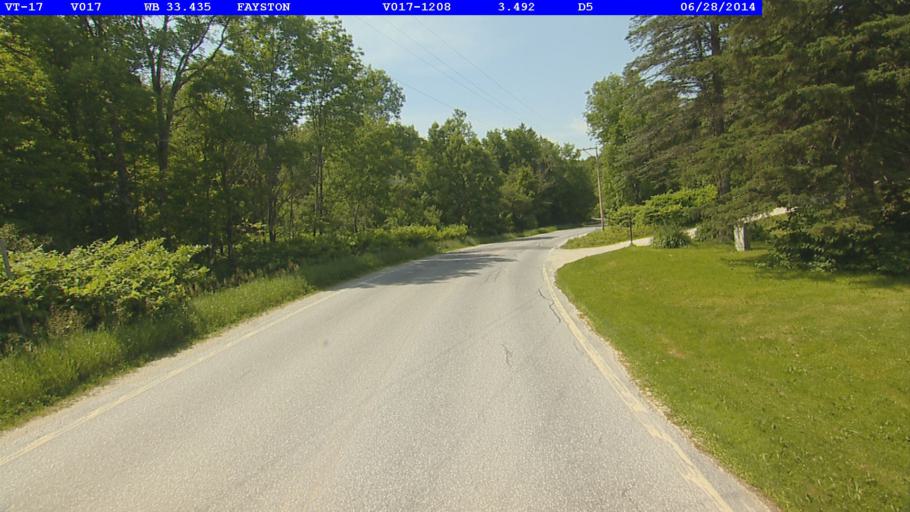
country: US
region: Vermont
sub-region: Washington County
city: Waterbury
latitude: 44.1907
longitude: -72.8844
